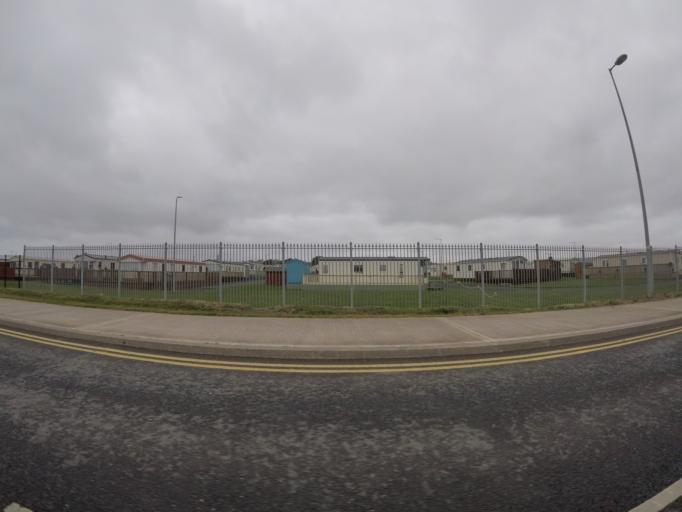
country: IE
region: Munster
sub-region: Waterford
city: Tra Mhor
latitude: 52.1622
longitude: -7.1354
